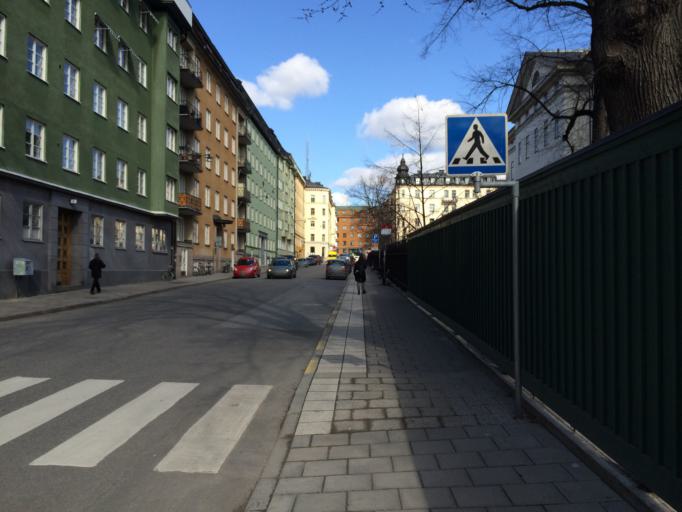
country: SE
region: Stockholm
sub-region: Stockholms Kommun
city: Stockholm
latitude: 59.3283
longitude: 18.0389
